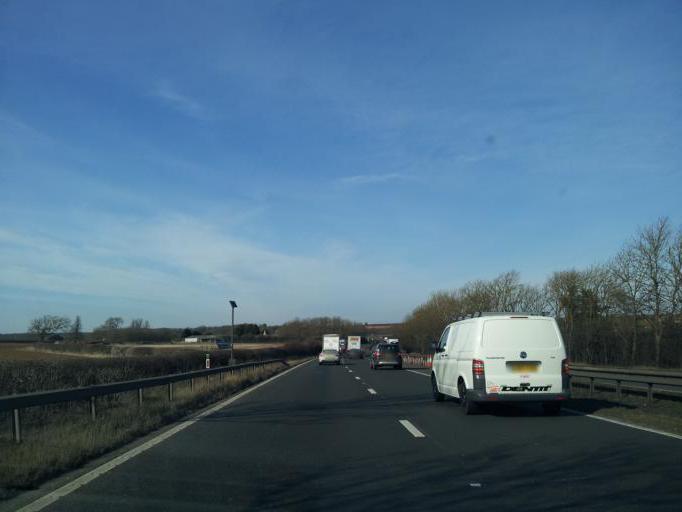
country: GB
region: England
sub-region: District of Rutland
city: Tickencote
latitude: 52.6649
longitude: -0.5235
